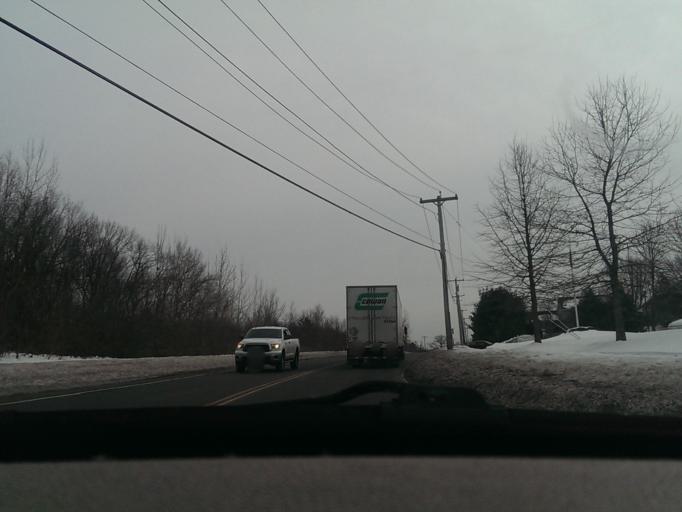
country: US
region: Massachusetts
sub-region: Hampden County
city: East Longmeadow
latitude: 42.0551
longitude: -72.5339
